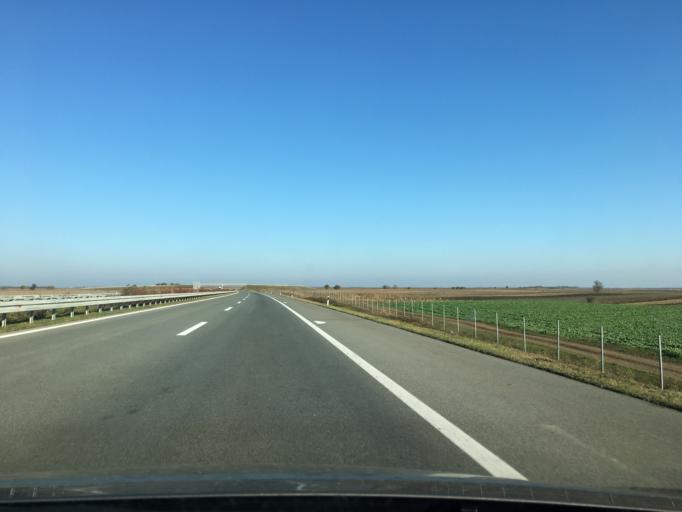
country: RS
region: Autonomna Pokrajina Vojvodina
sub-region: Severnobacki Okrug
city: Mali Igos
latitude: 45.6598
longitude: 19.7259
